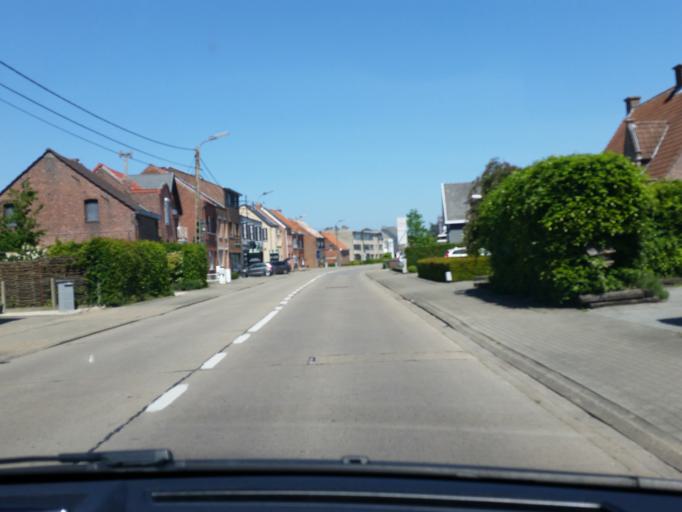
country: BE
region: Flanders
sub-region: Provincie Antwerpen
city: Mechelen
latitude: 51.0466
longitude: 4.5048
